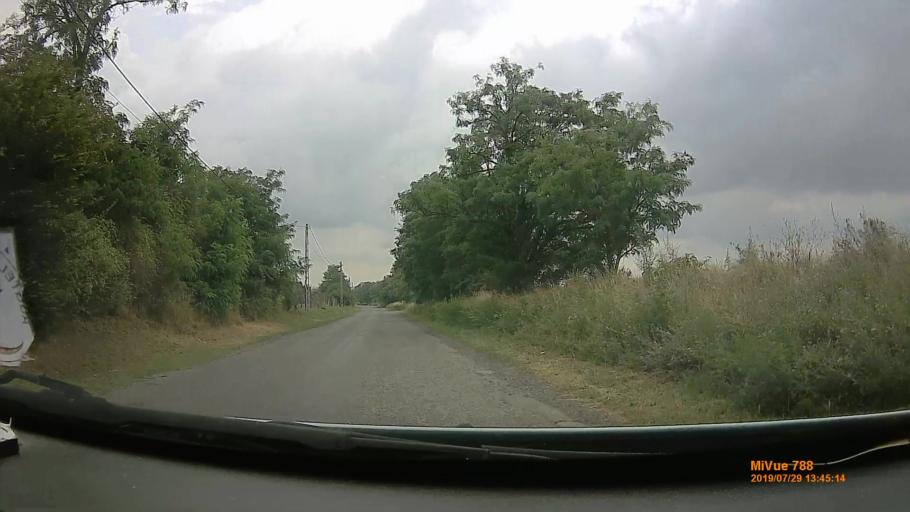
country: HU
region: Somogy
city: Balatonfoldvar
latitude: 46.7929
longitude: 17.9394
